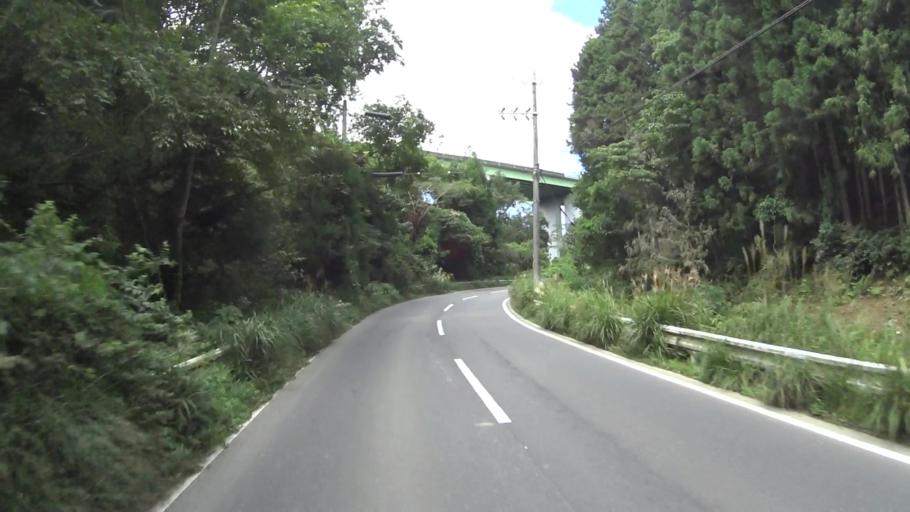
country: JP
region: Shiga Prefecture
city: Otsu-shi
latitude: 34.9203
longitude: 135.8847
